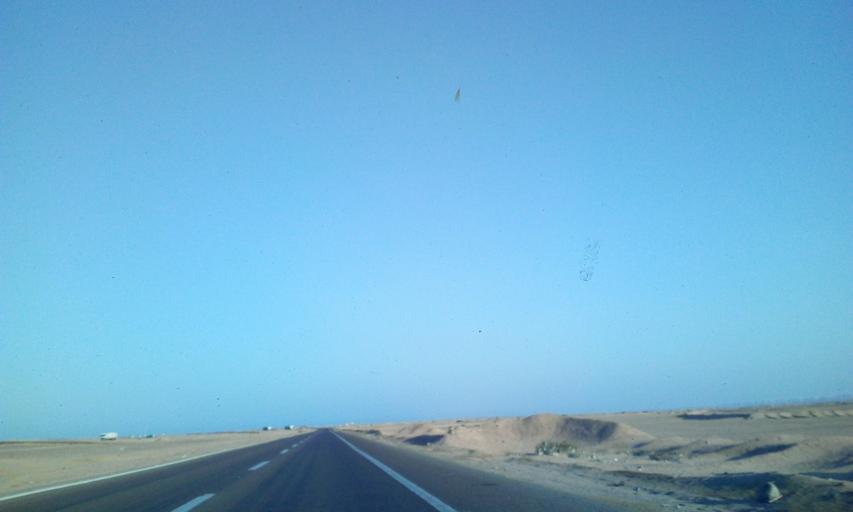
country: EG
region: South Sinai
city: Tor
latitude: 28.2787
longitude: 33.1230
